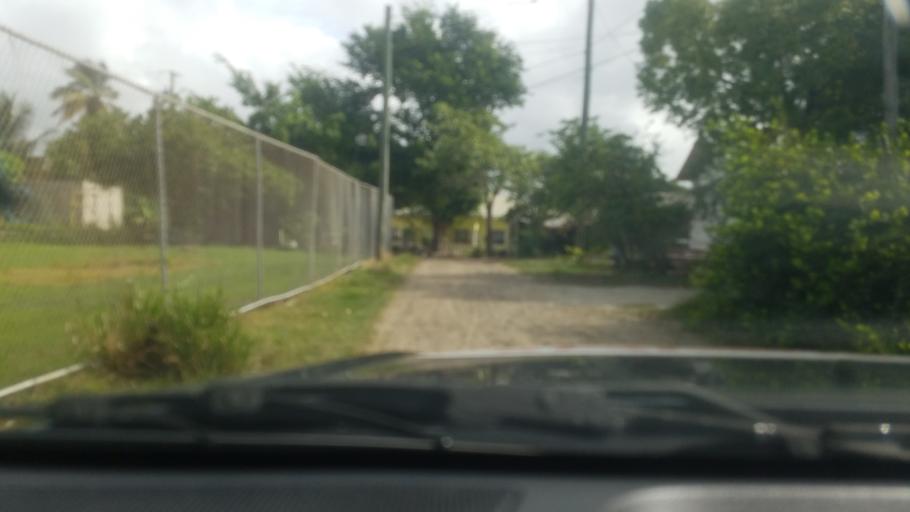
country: LC
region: Micoud Quarter
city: Micoud
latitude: 13.7970
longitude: -60.9194
